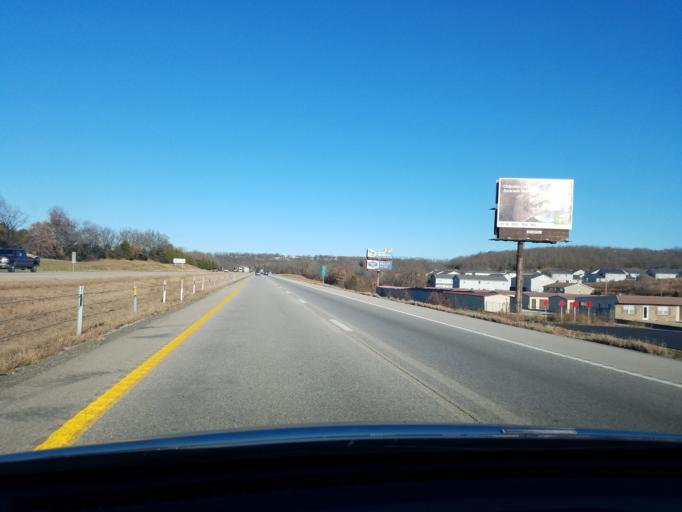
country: US
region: Missouri
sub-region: Pulaski County
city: Waynesville
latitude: 37.8123
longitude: -92.2098
